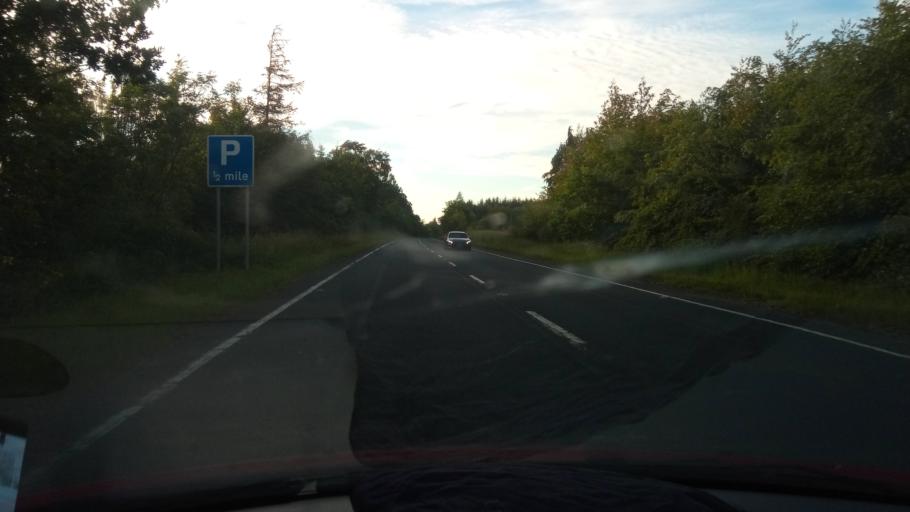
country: GB
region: Scotland
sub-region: Dumfries and Galloway
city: Langholm
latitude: 55.0803
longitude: -2.9600
